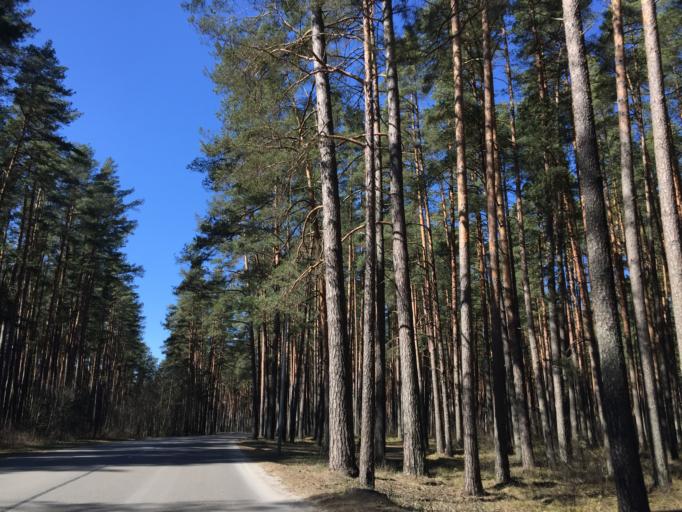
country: LV
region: Jurmala
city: Jurmala
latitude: 56.9424
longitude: 23.7139
